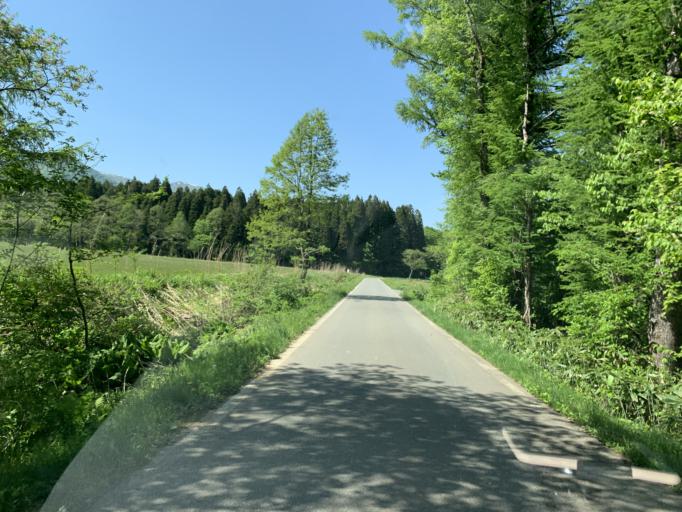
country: JP
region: Iwate
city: Shizukuishi
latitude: 39.5638
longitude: 140.8315
